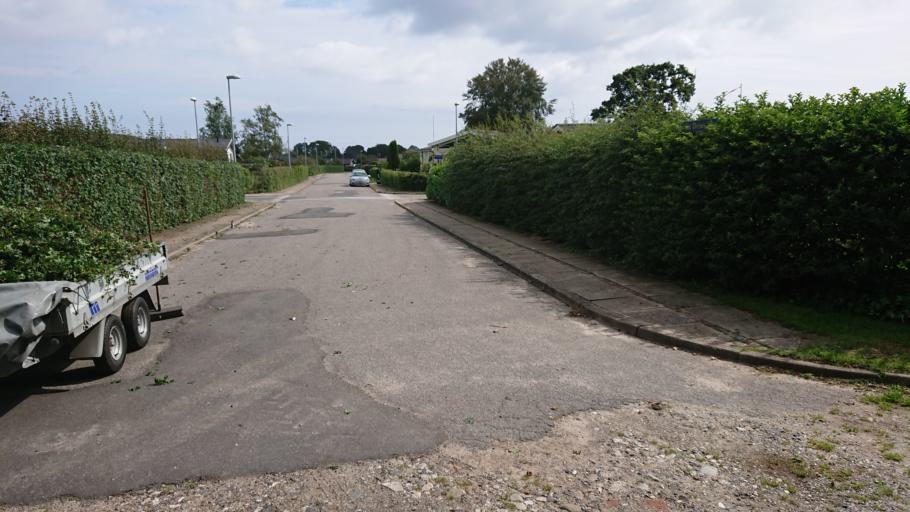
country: DK
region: North Denmark
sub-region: Frederikshavn Kommune
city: Saeby
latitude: 57.3418
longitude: 10.5089
